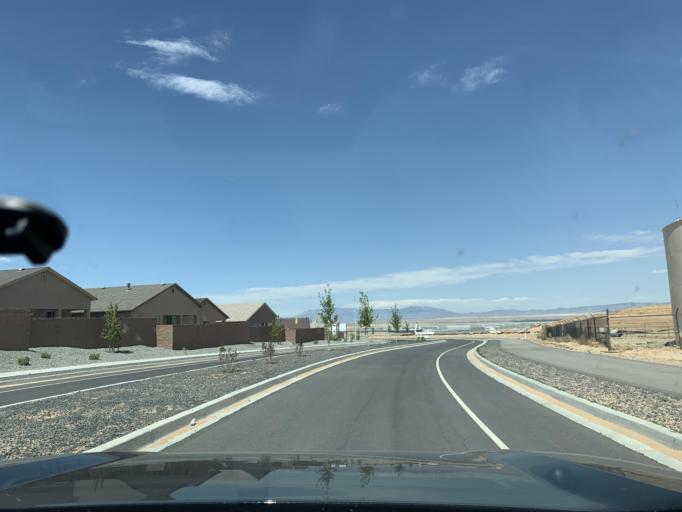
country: US
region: New Mexico
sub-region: Valencia County
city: Los Lunas
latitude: 34.8184
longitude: -106.7985
